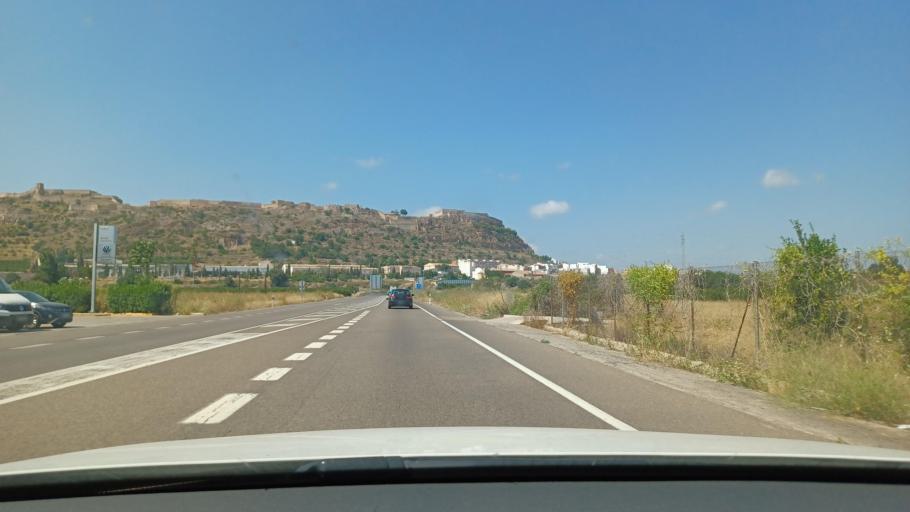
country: ES
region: Valencia
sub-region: Provincia de Valencia
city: Sagunto
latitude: 39.6679
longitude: -0.2780
